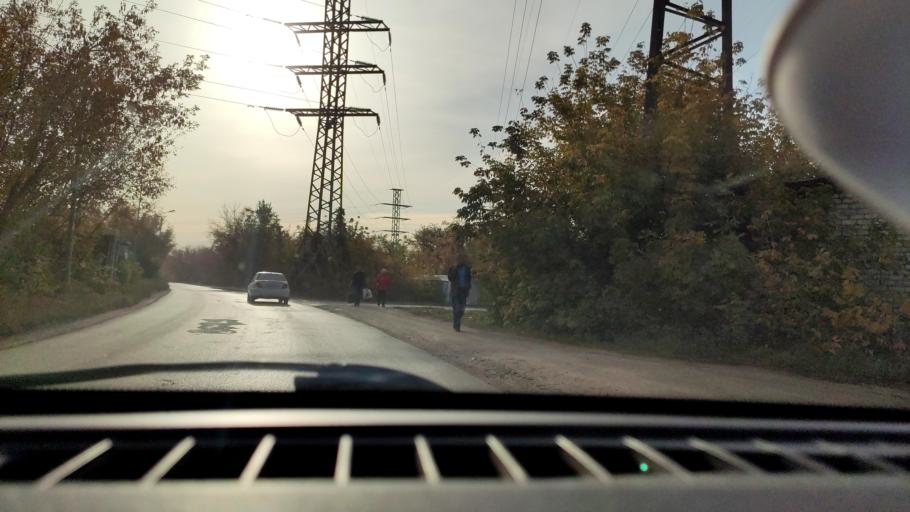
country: RU
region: Samara
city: Petra-Dubrava
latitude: 53.2953
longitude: 50.2904
